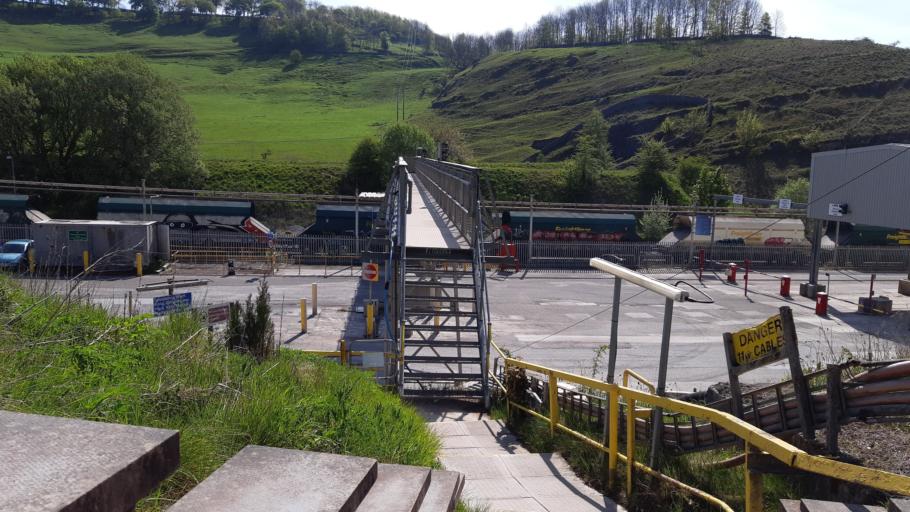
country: GB
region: England
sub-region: Derbyshire
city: Buxton
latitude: 53.2702
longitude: -1.8511
